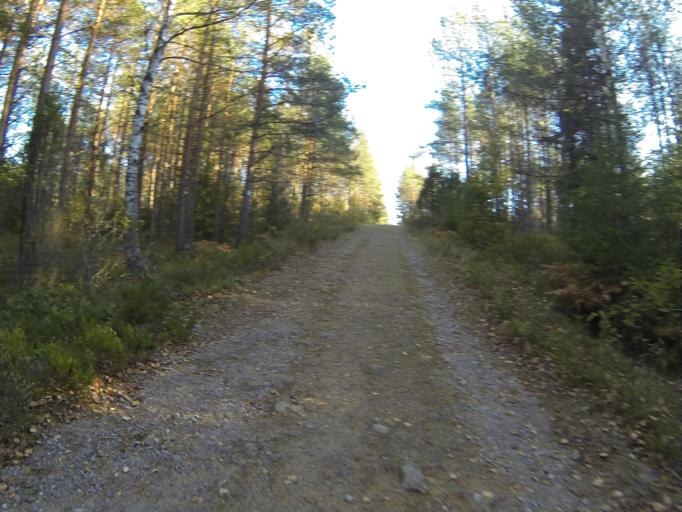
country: FI
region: Varsinais-Suomi
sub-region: Salo
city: Saerkisalo
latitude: 60.2197
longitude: 22.9304
